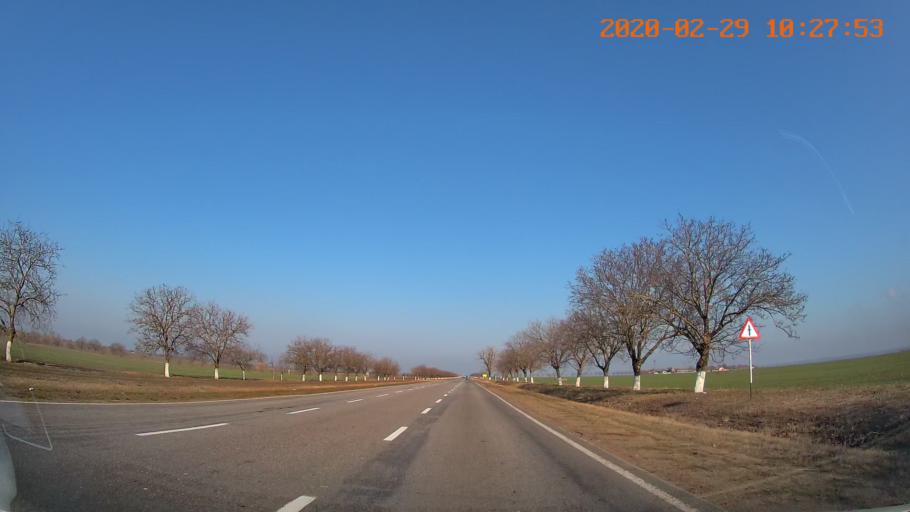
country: MD
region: Telenesti
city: Tiraspolul Nou
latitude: 46.9025
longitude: 29.5951
